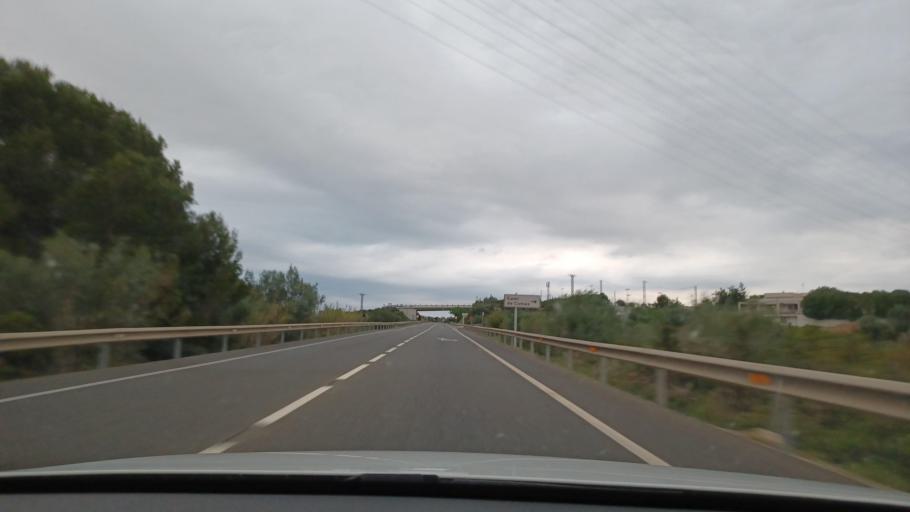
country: ES
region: Catalonia
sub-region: Provincia de Tarragona
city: Amposta
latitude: 40.7131
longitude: 0.5649
